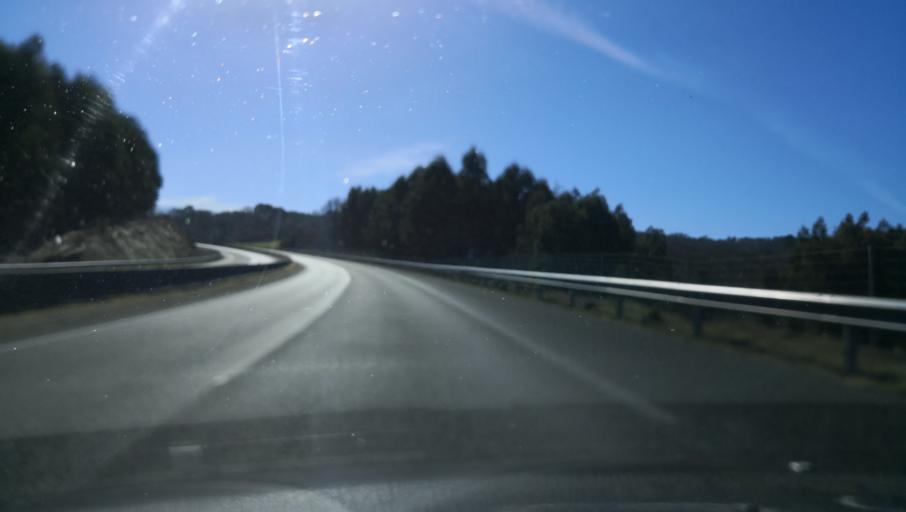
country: ES
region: Galicia
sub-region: Provincia de Pontevedra
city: Lalin
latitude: 42.6644
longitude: -8.1471
